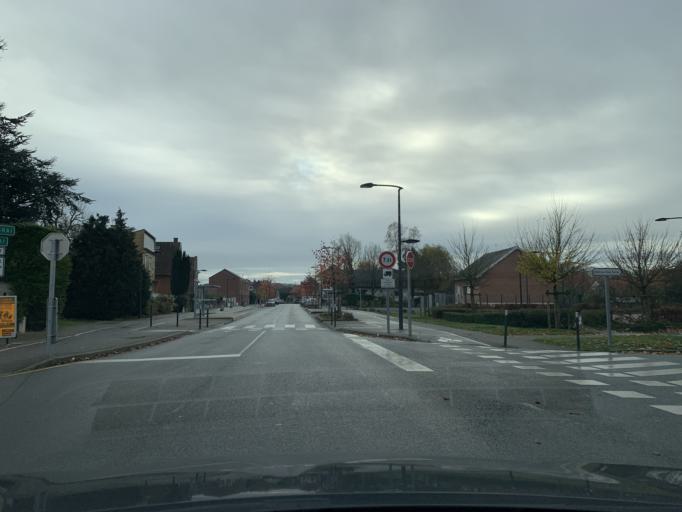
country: FR
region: Nord-Pas-de-Calais
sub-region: Departement du Nord
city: Cantin
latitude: 50.3130
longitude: 3.1227
